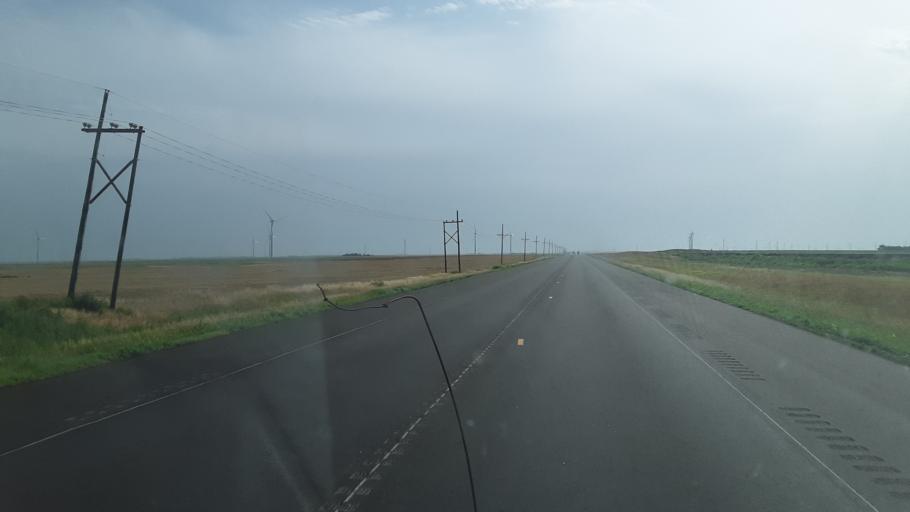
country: US
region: Kansas
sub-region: Ford County
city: Dodge City
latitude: 37.7972
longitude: -99.8638
